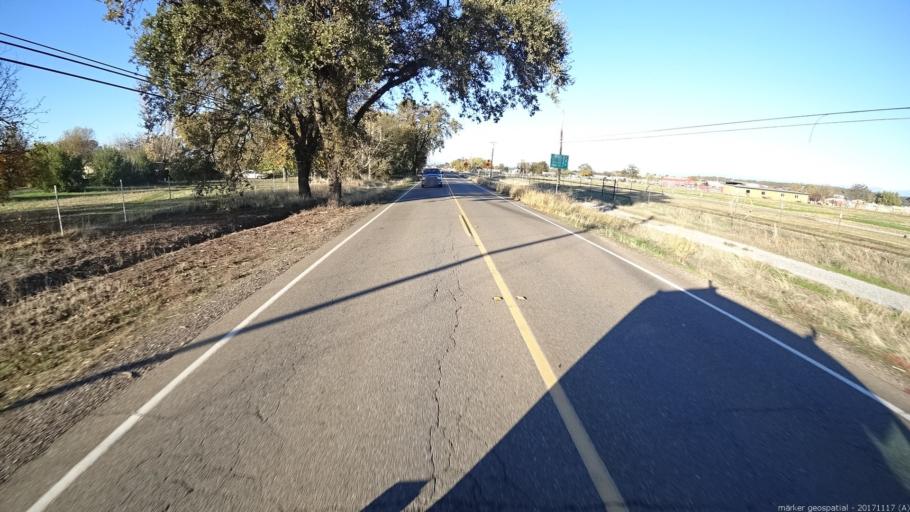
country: US
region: California
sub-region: Shasta County
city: Anderson
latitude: 40.4734
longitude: -122.2420
